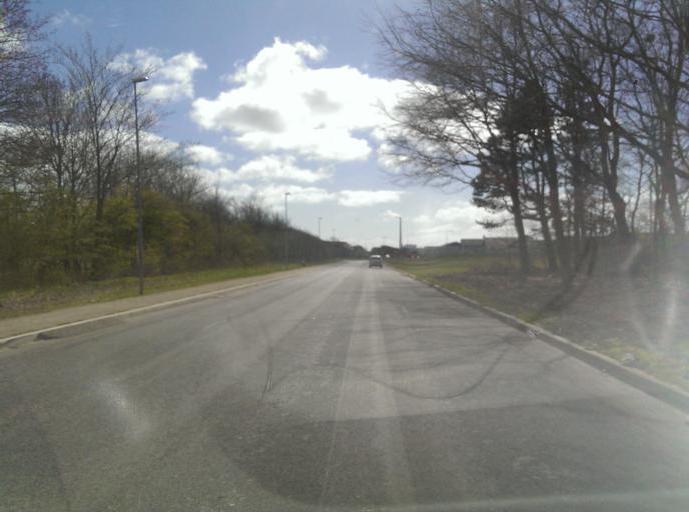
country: DK
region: South Denmark
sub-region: Esbjerg Kommune
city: Esbjerg
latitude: 55.4855
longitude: 8.4223
